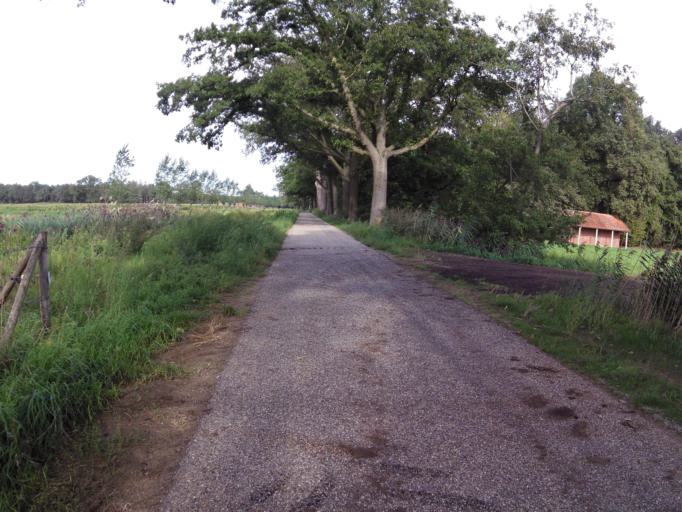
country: NL
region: Gelderland
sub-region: Oude IJsselstreek
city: Varsseveld
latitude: 51.9584
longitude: 6.4524
